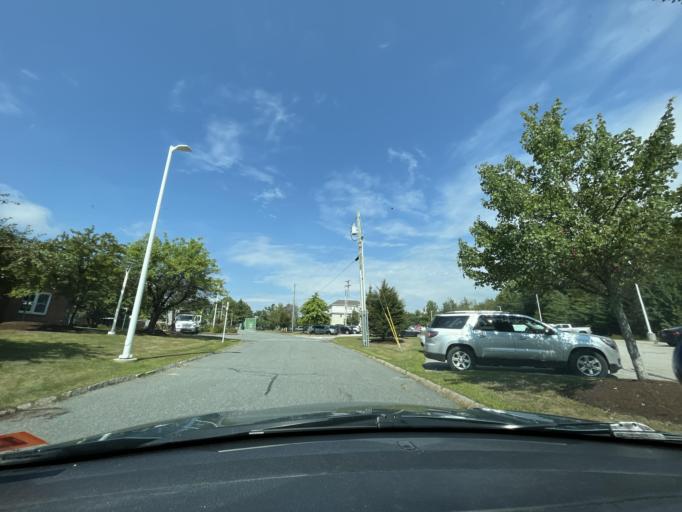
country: US
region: New Hampshire
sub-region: Merrimack County
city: New London
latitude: 43.4208
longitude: -71.9991
